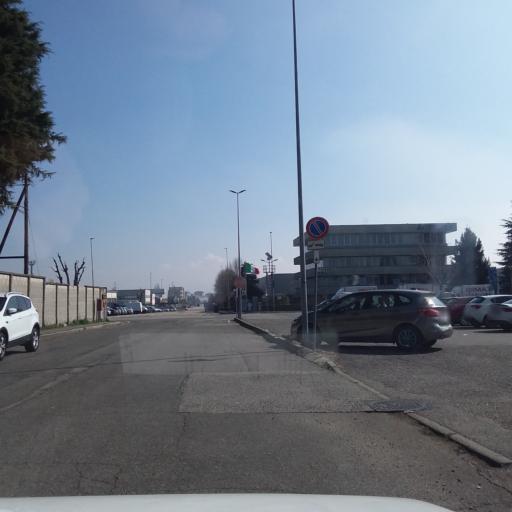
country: IT
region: Piedmont
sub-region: Provincia di Torino
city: Tetti Neirotti
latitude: 45.0633
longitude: 7.5494
